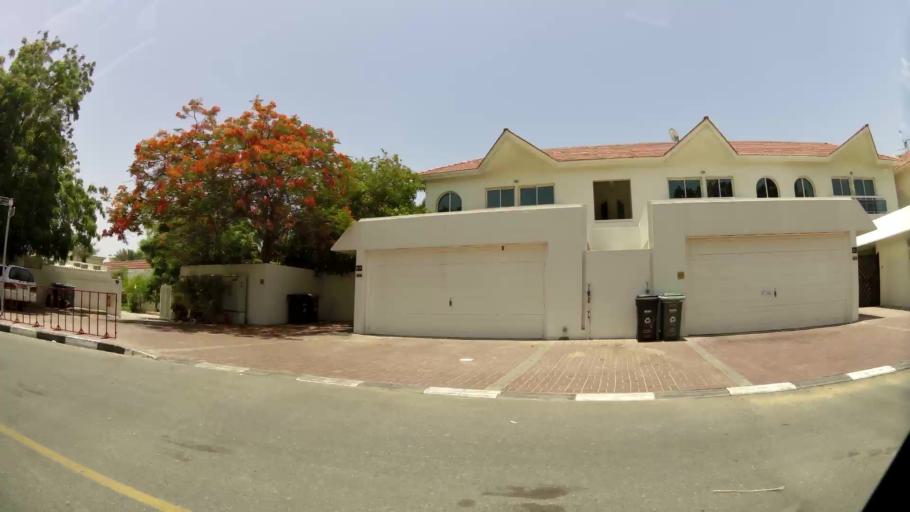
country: AE
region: Dubai
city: Dubai
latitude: 25.1772
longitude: 55.2379
